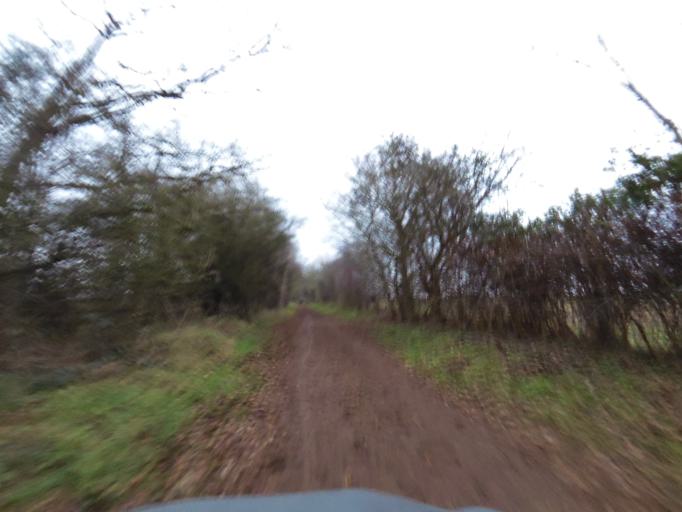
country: GB
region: England
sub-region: Norfolk
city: Horsford
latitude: 52.6981
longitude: 1.2009
